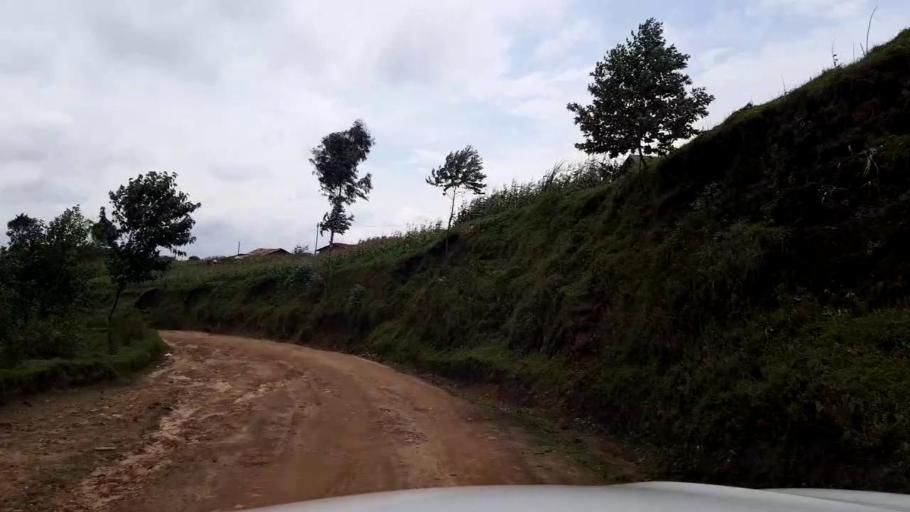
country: RW
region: Western Province
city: Kibuye
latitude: -1.9538
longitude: 29.4193
